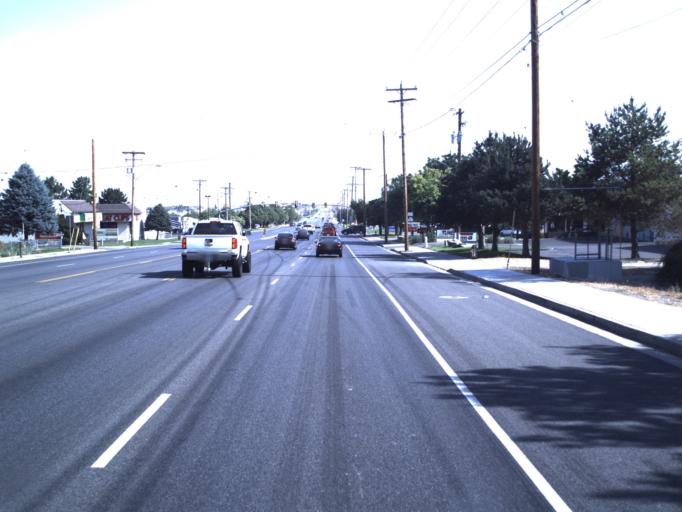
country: US
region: Utah
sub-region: Salt Lake County
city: West Valley City
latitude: 40.6946
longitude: -112.0248
